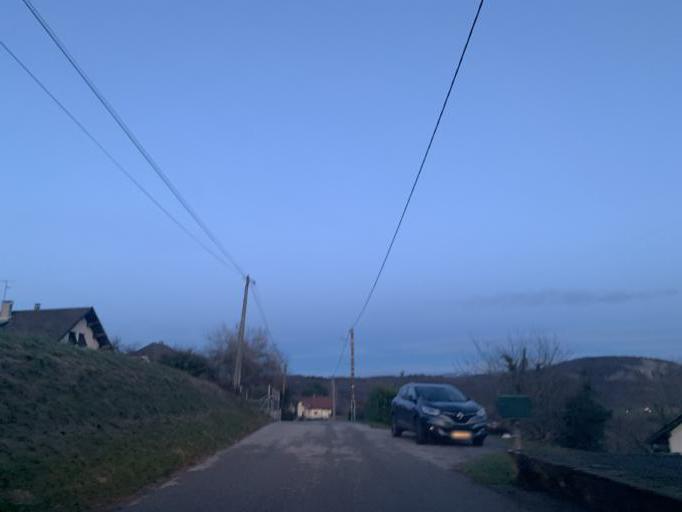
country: FR
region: Rhone-Alpes
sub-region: Departement de l'Ain
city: Belley
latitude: 45.7702
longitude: 5.6997
